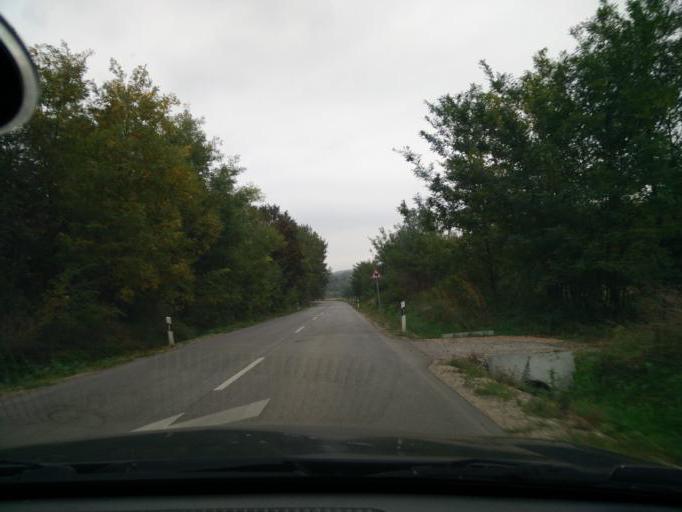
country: HU
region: Komarom-Esztergom
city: Bajna
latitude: 47.6963
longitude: 18.6155
